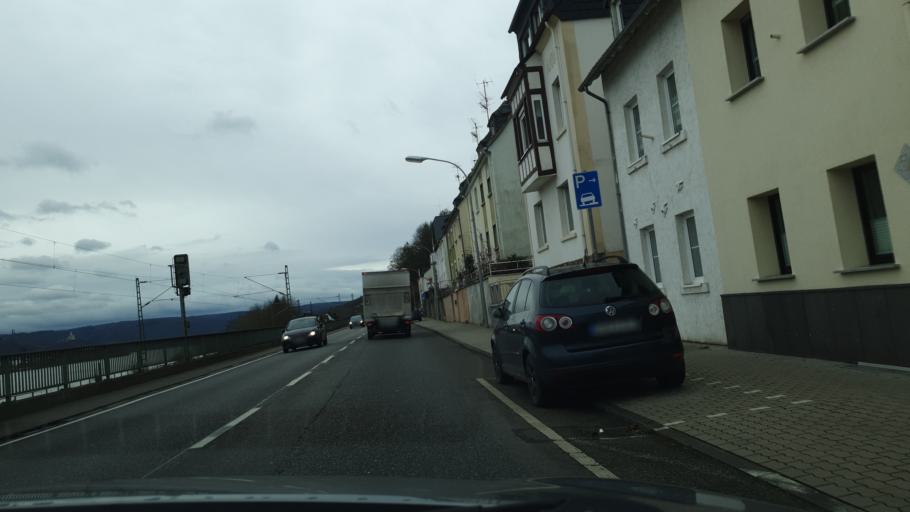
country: DE
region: Rheinland-Pfalz
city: Lahnstein
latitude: 50.3019
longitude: 7.5949
